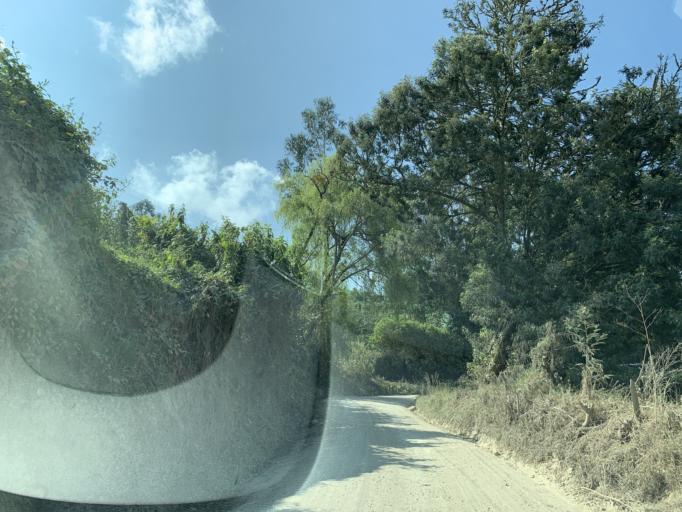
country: CO
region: Boyaca
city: Turmeque
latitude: 5.2906
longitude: -73.5018
